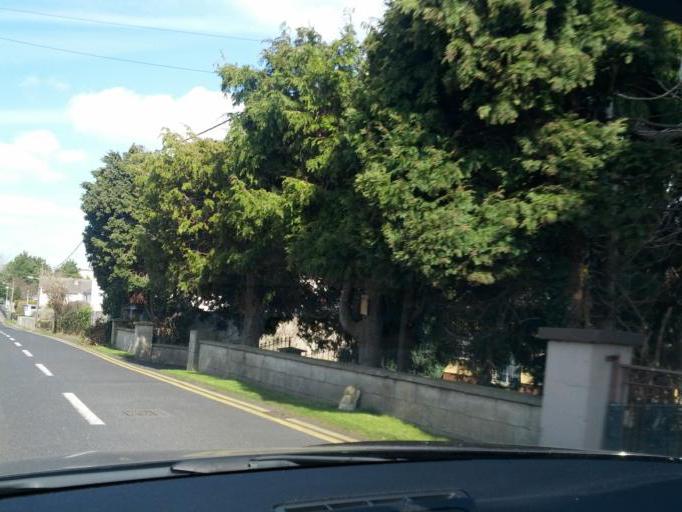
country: IE
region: Leinster
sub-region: Kildare
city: Leixlip
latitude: 53.3672
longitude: -6.5077
